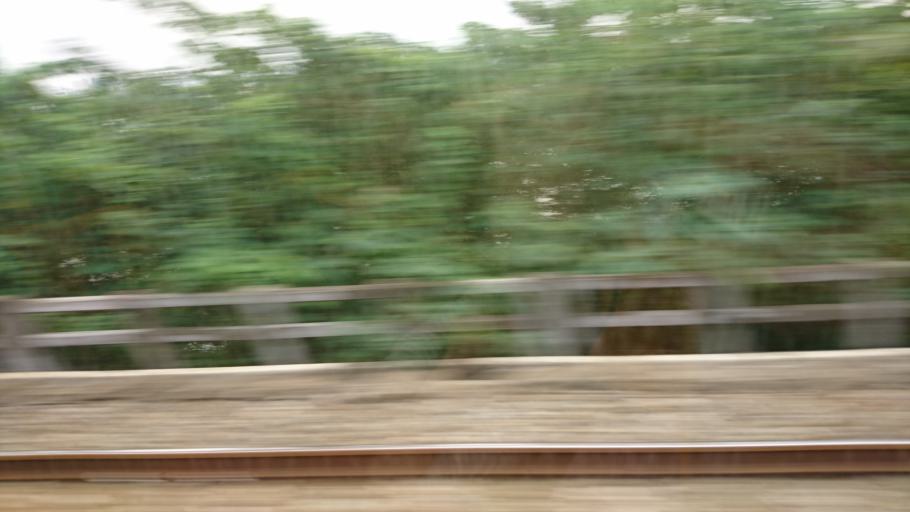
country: TW
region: Taiwan
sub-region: Hsinchu
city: Zhubei
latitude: 24.8545
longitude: 121.0089
